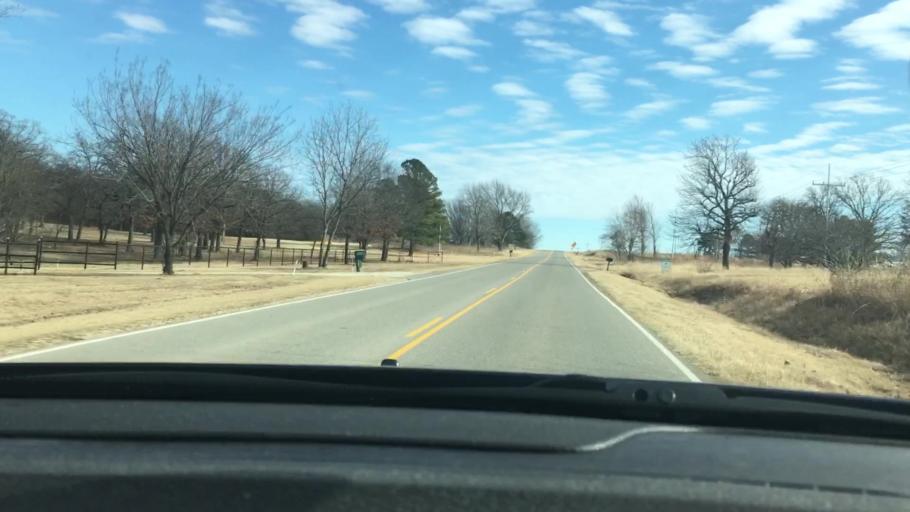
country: US
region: Oklahoma
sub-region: Pontotoc County
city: Ada
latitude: 34.7848
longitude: -96.7899
